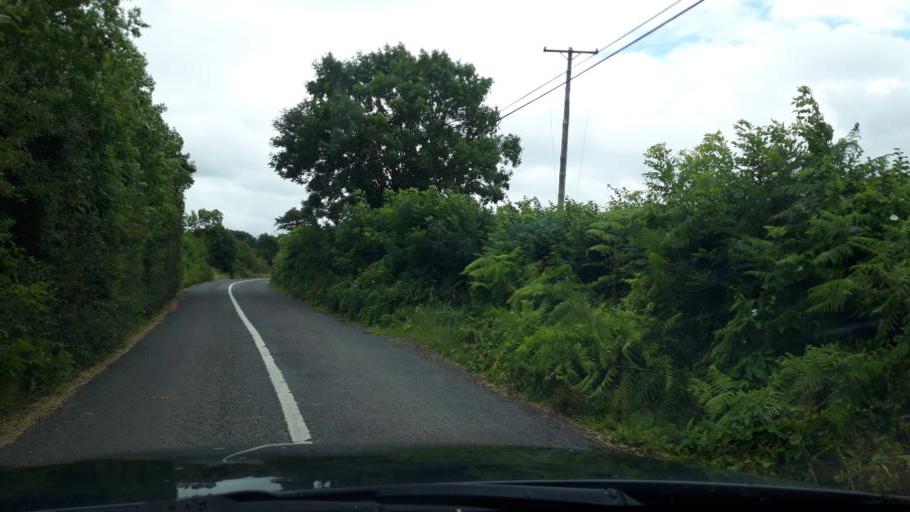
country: IE
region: Munster
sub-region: County Cork
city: Castlemartyr
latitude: 52.1295
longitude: -8.0024
